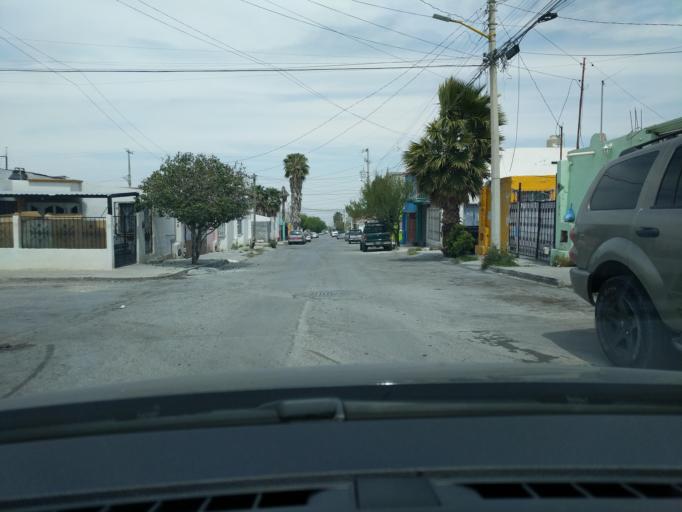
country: MX
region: Coahuila
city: Saltillo
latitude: 25.4073
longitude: -100.9379
